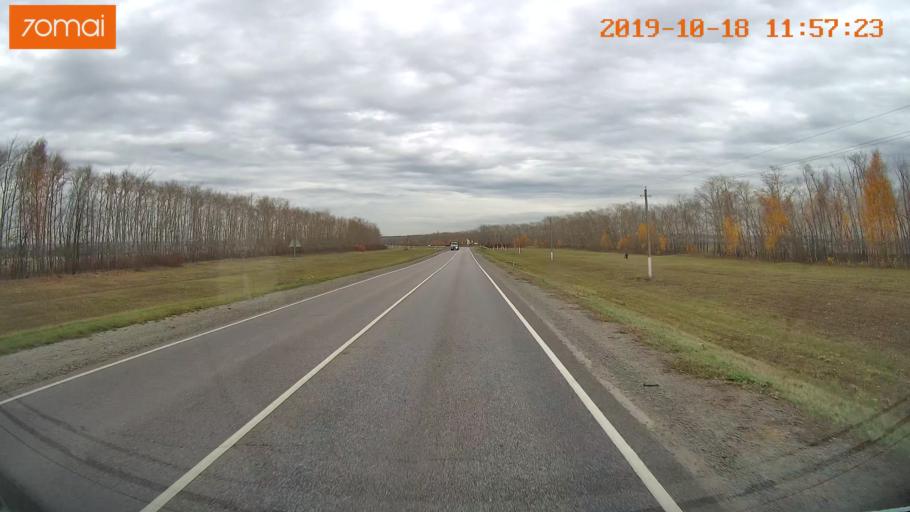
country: RU
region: Rjazan
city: Mikhaylov
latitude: 54.2663
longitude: 39.1424
